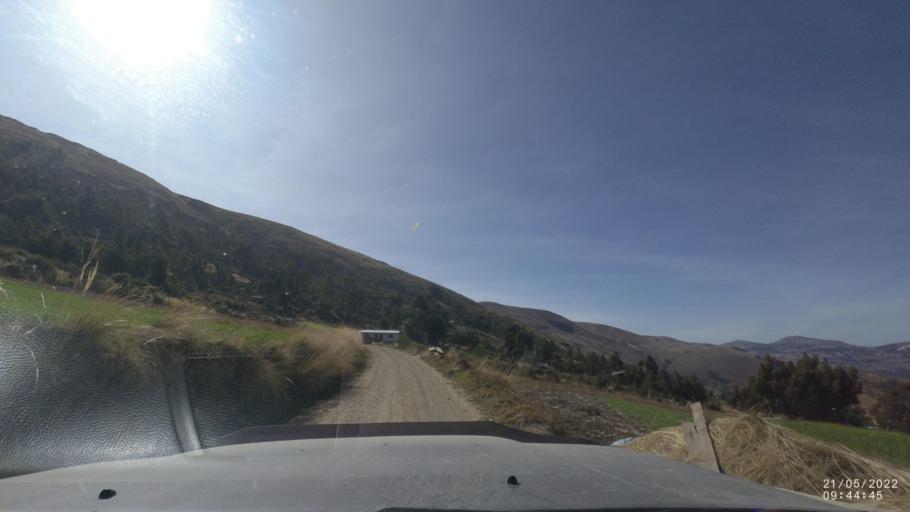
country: BO
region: Cochabamba
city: Colomi
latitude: -17.3430
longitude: -66.0031
